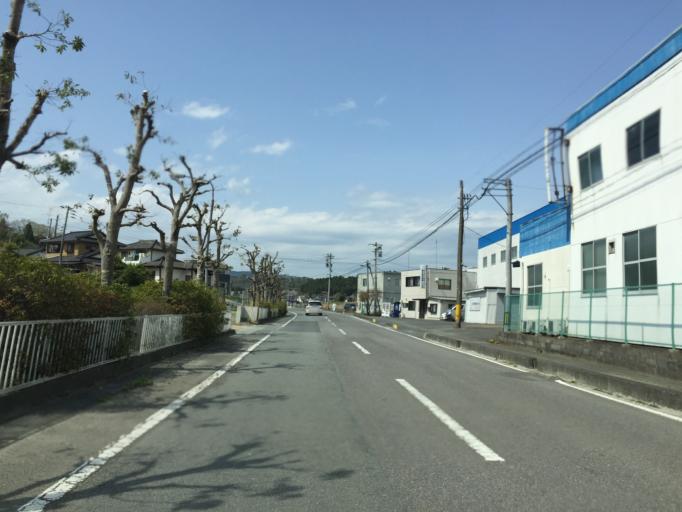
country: JP
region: Fukushima
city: Iwaki
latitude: 37.1602
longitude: 140.9750
